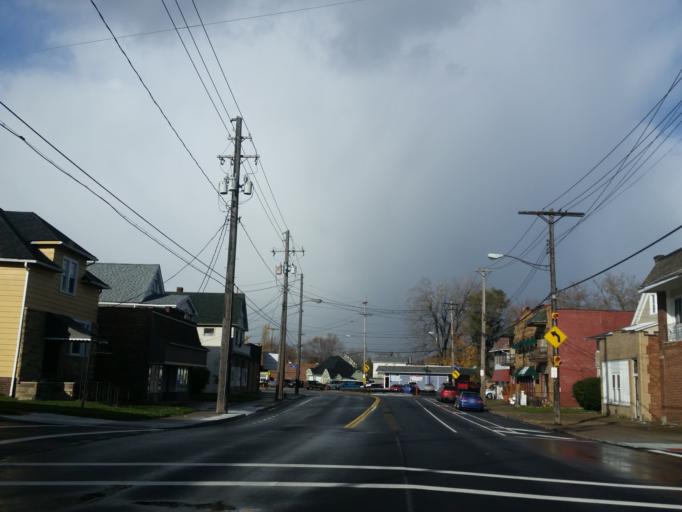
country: US
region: Ohio
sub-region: Cuyahoga County
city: Brooklyn Heights
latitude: 41.4340
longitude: -81.6971
